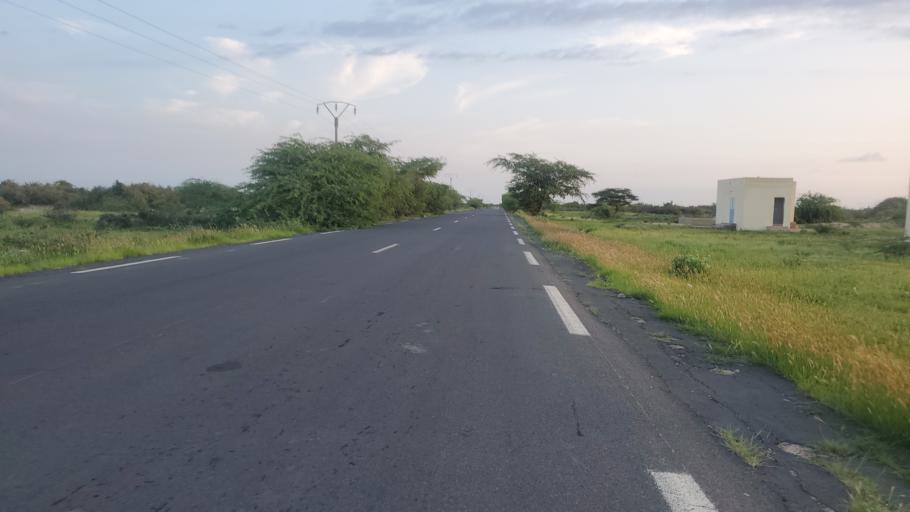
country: SN
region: Saint-Louis
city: Saint-Louis
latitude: 16.1319
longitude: -16.4123
